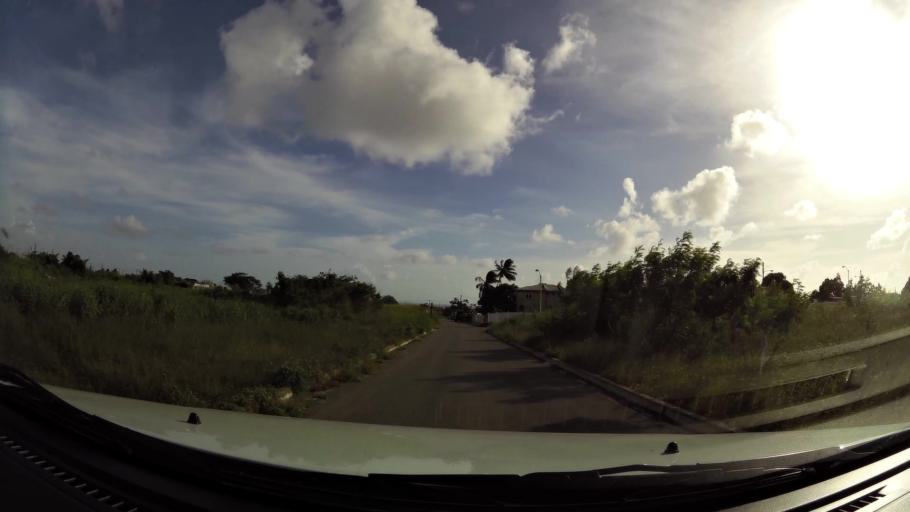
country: BB
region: Christ Church
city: Oistins
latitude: 13.0845
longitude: -59.5607
